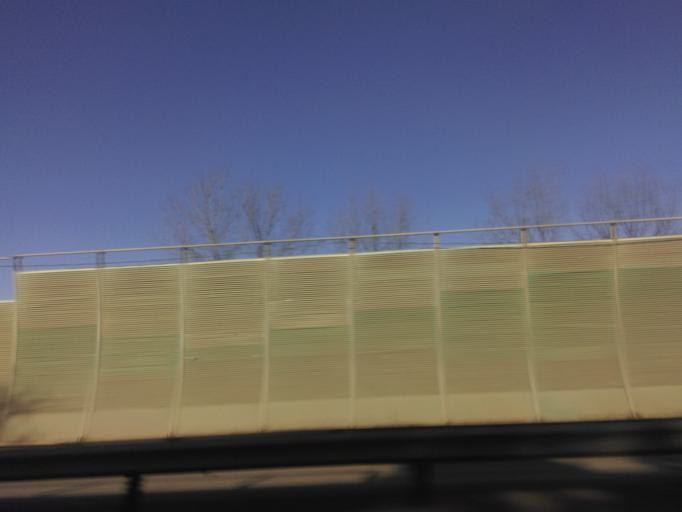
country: RU
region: Moscow
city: Novo-Peredelkino
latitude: 55.6745
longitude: 37.3167
